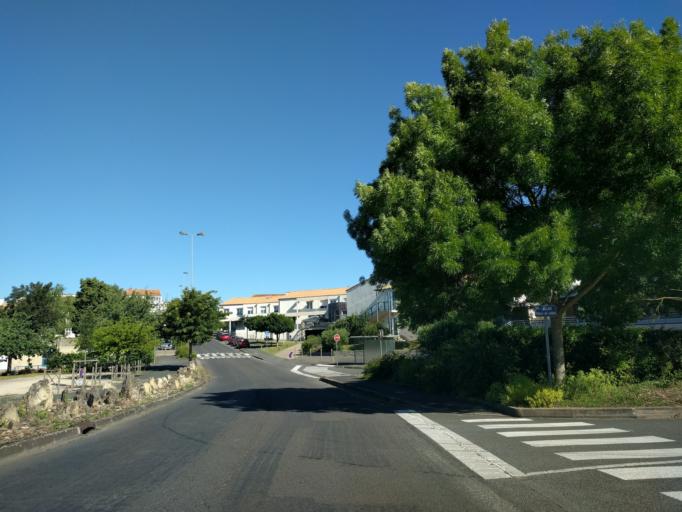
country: FR
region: Poitou-Charentes
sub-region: Departement des Deux-Sevres
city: Niort
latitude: 46.3394
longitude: -0.4365
